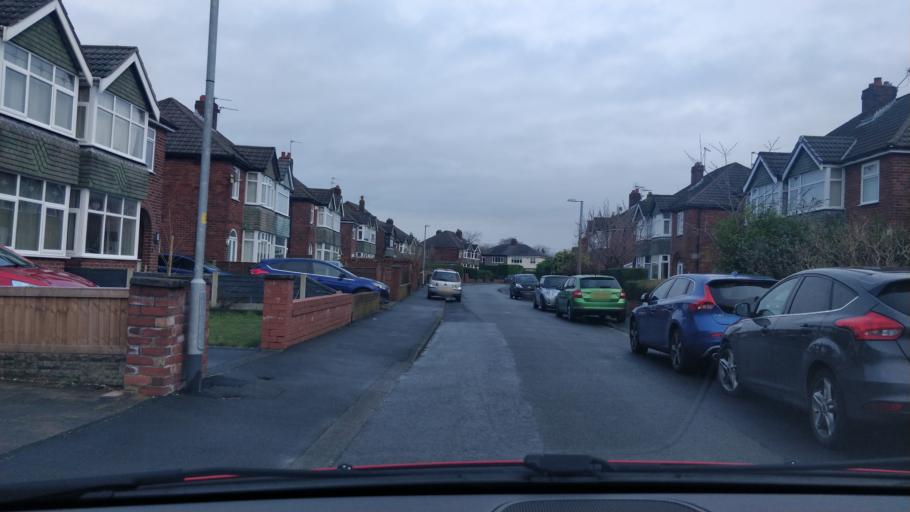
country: GB
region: England
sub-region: Lancashire
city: Preston
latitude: 53.7438
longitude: -2.7338
